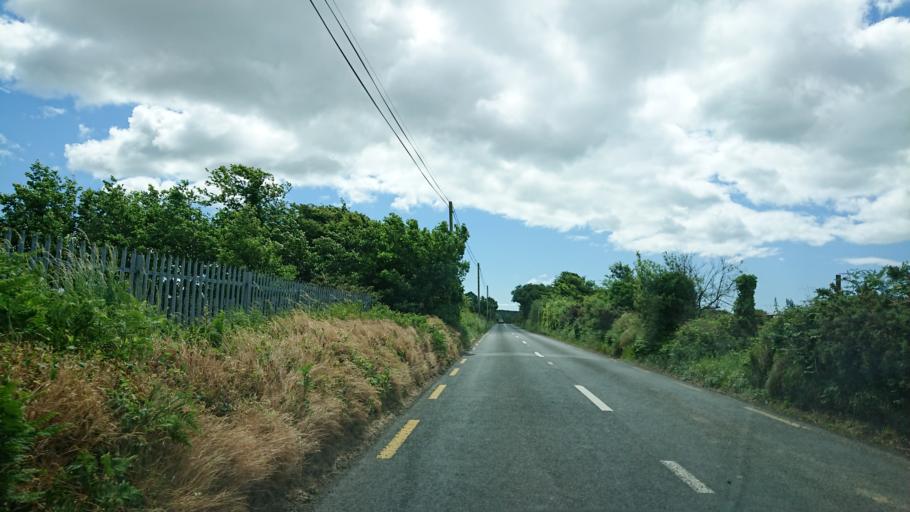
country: IE
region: Munster
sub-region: Waterford
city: Tra Mhor
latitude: 52.1933
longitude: -7.1861
